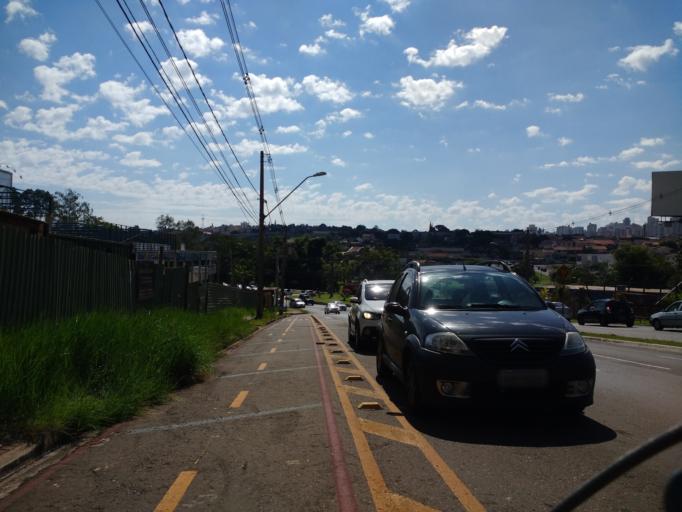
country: BR
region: Parana
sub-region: Londrina
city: Londrina
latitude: -23.3257
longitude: -51.1760
